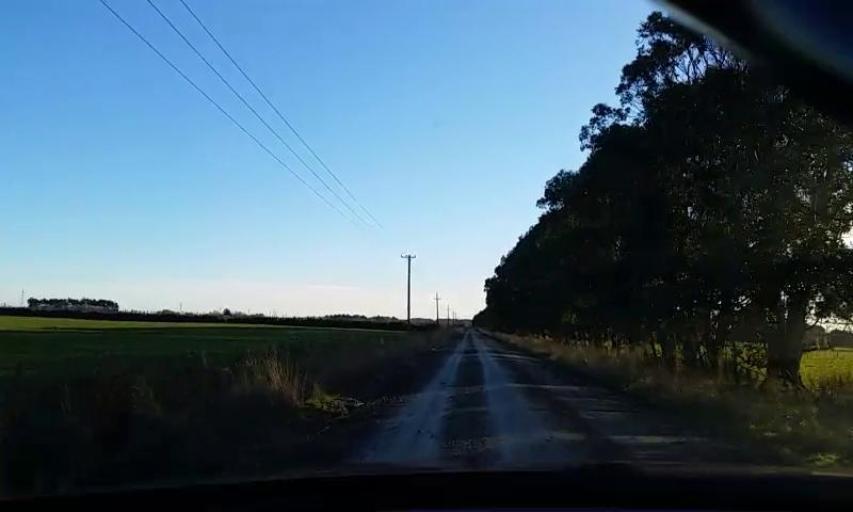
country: NZ
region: Southland
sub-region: Invercargill City
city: Invercargill
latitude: -46.2918
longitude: 168.4506
